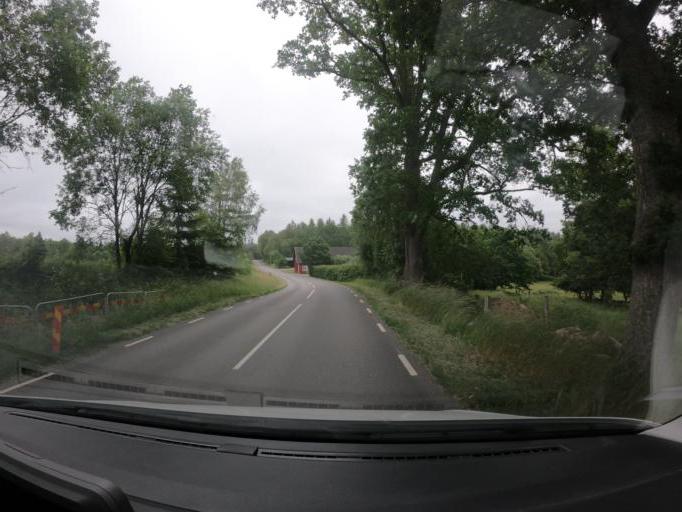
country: SE
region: Skane
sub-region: Perstorps Kommun
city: Perstorp
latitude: 56.0762
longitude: 13.3962
